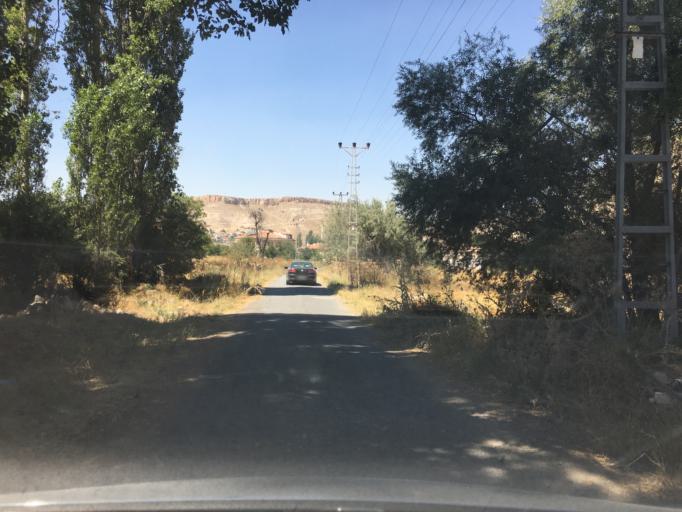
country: TR
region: Nevsehir
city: Urgub
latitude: 38.4676
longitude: 34.9639
